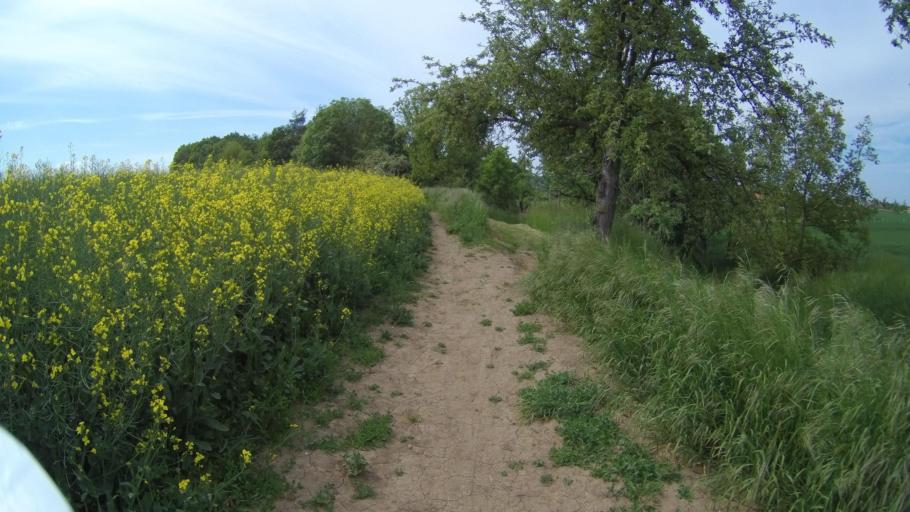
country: CZ
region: Central Bohemia
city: Libeznice
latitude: 50.1727
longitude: 14.4791
